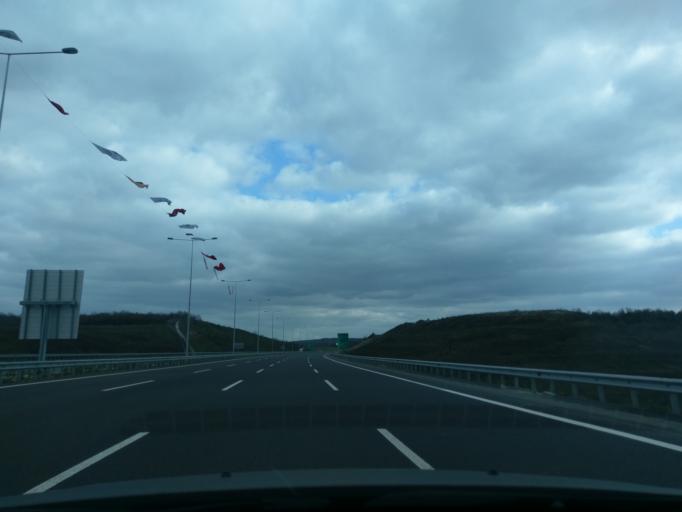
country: TR
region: Istanbul
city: Kemerburgaz
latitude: 41.2379
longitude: 28.8237
